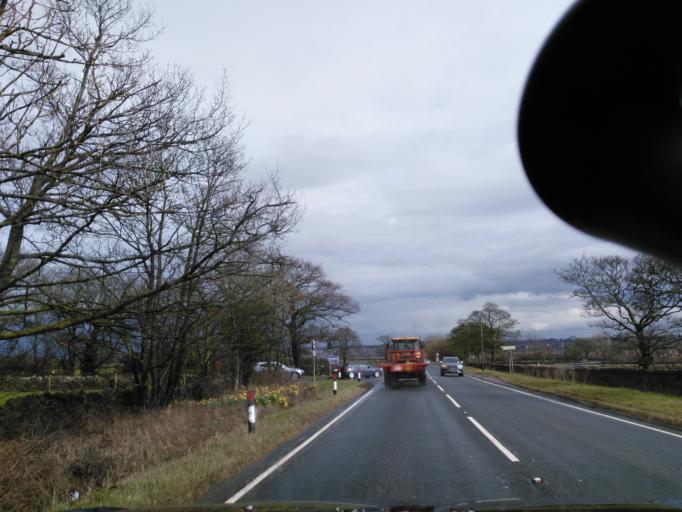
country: GB
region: England
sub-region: North Yorkshire
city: Harrogate
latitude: 54.0089
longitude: -1.5908
